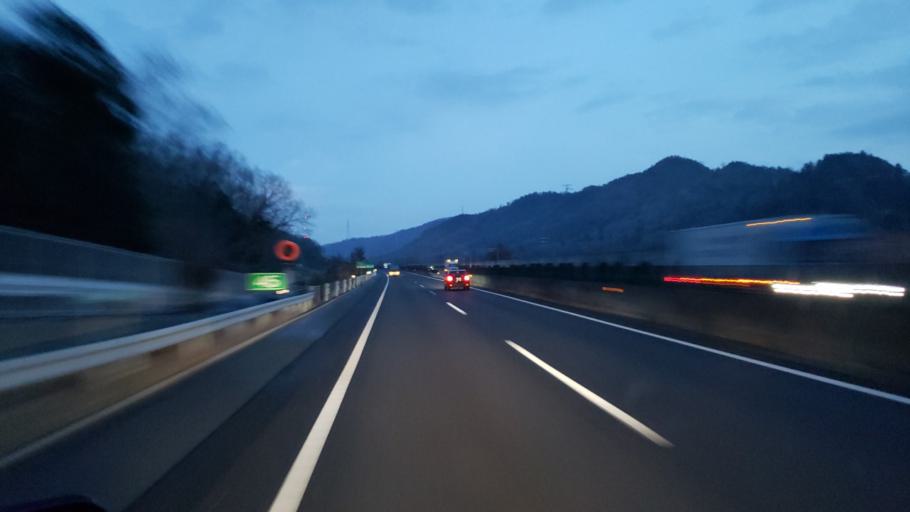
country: JP
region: Hyogo
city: Kakogawacho-honmachi
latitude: 34.8515
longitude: 134.7905
